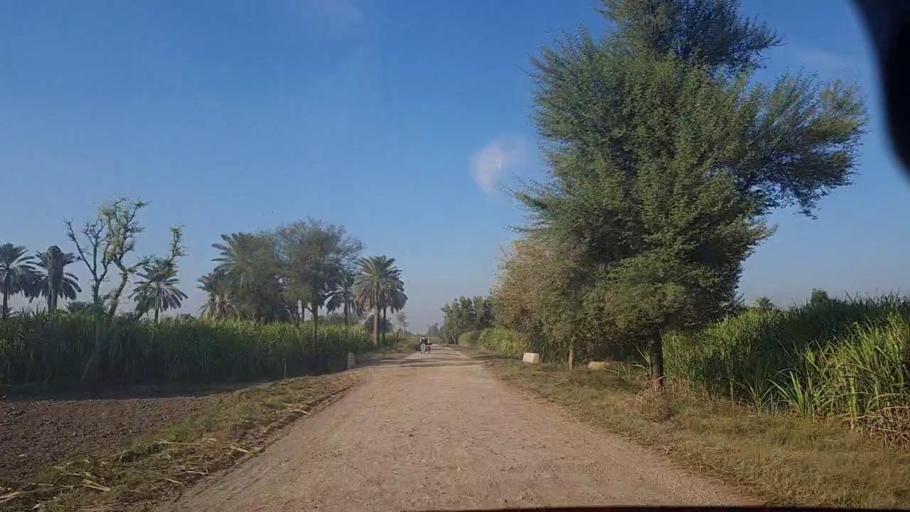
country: PK
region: Sindh
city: Sobhadero
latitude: 27.3943
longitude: 68.4198
